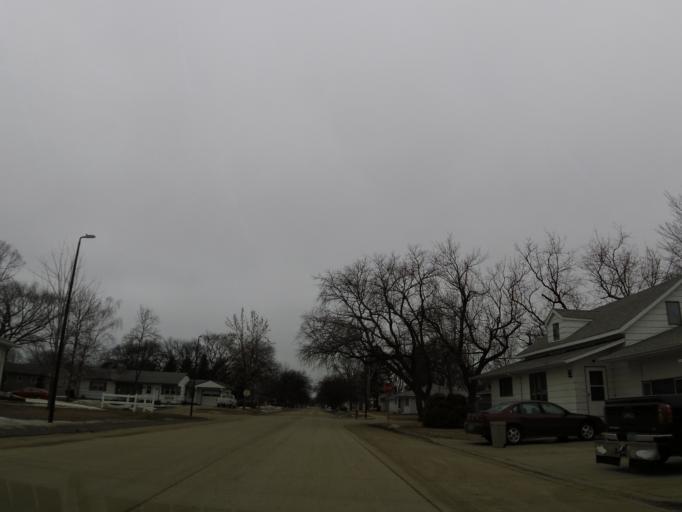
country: US
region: North Dakota
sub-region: Walsh County
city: Grafton
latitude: 48.4105
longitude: -97.4105
